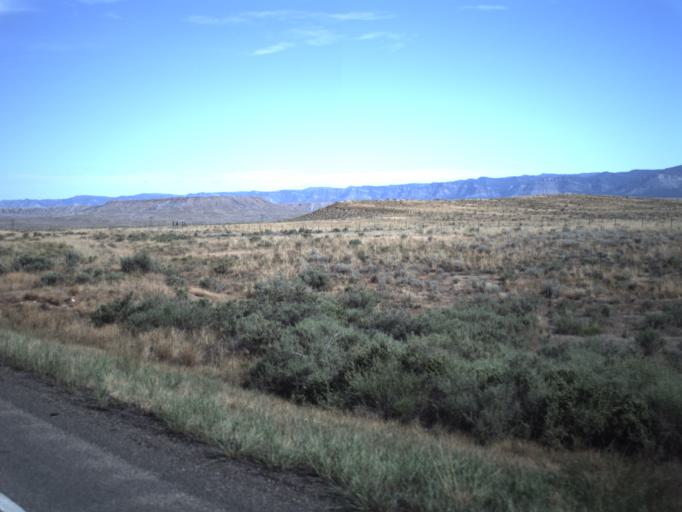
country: US
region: Utah
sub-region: Carbon County
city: East Carbon City
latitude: 39.4388
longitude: -110.4616
